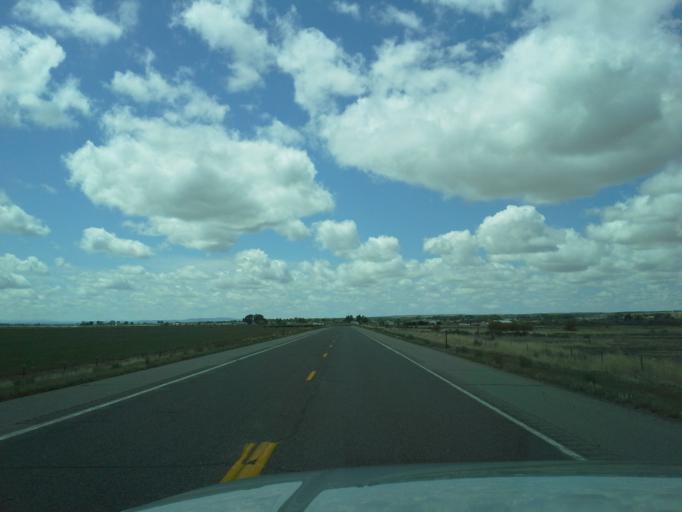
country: US
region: Wyoming
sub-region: Washakie County
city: Worland
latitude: 44.1072
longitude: -107.9116
